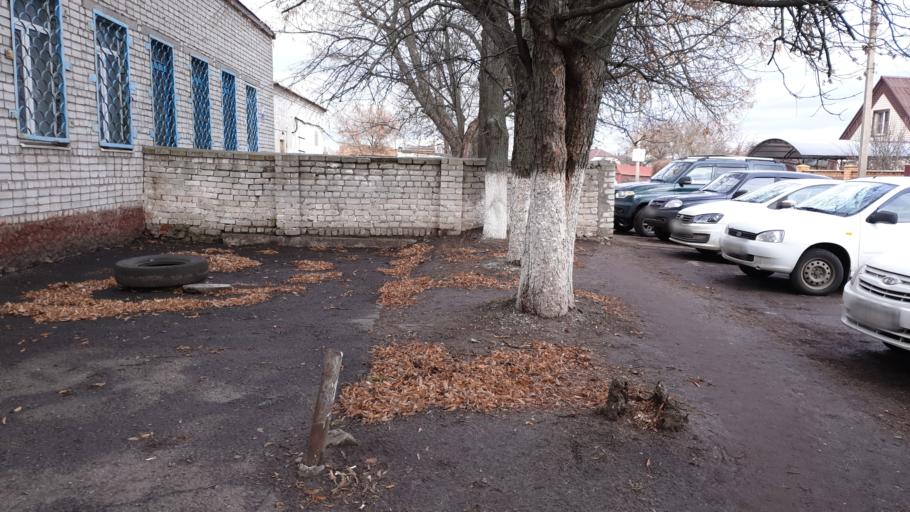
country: RU
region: Kursk
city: Voroshnevo
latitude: 51.6694
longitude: 36.0946
